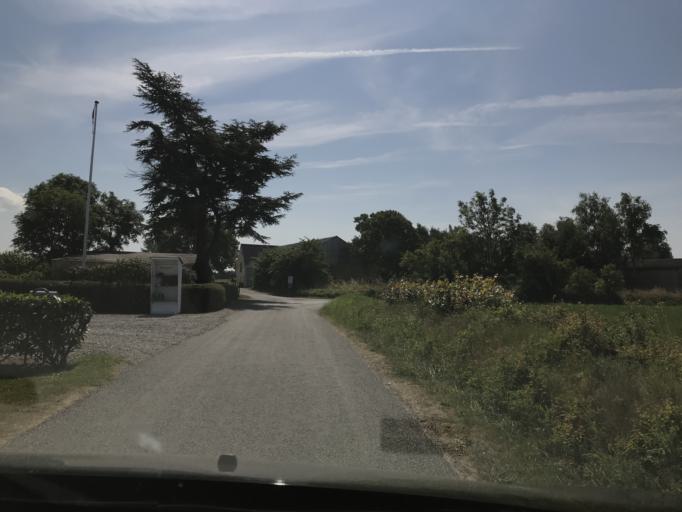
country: DK
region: South Denmark
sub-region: AEro Kommune
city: AEroskobing
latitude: 54.9303
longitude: 10.2851
